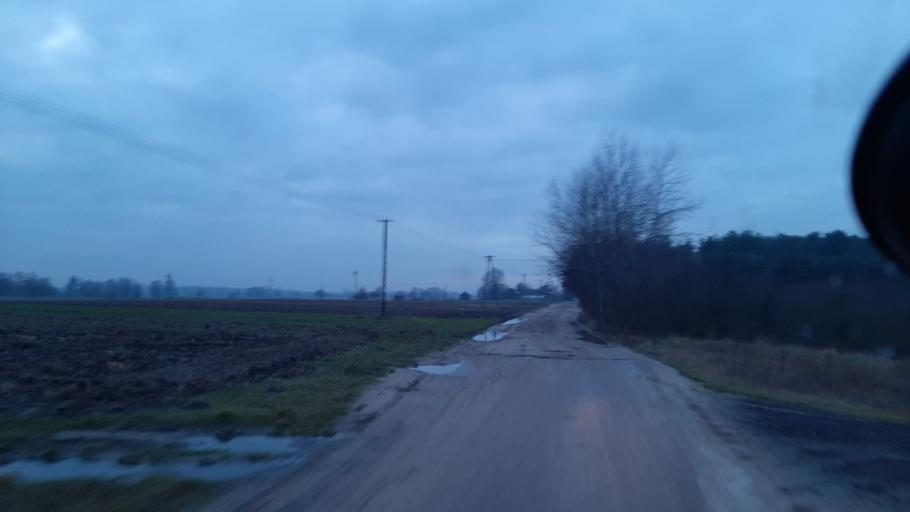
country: PL
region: Lublin Voivodeship
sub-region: Powiat lubartowski
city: Firlej
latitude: 51.5881
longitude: 22.5379
